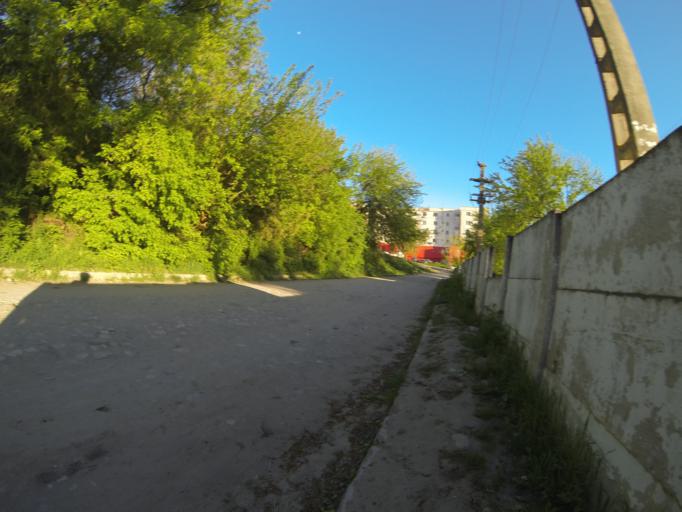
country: RO
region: Dolj
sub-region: Comuna Segarcea
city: Segarcea
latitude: 44.0943
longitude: 23.7443
